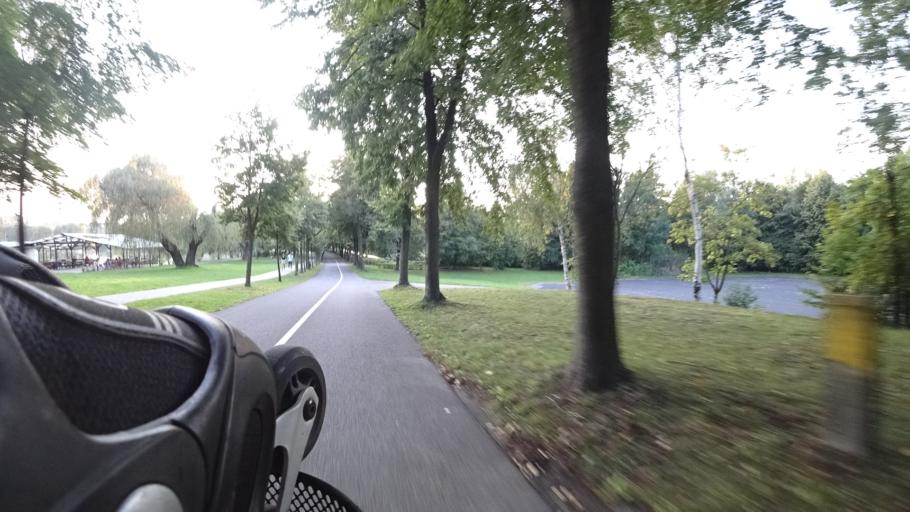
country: PL
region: Silesian Voivodeship
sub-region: Katowice
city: Katowice
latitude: 50.2488
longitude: 19.0476
